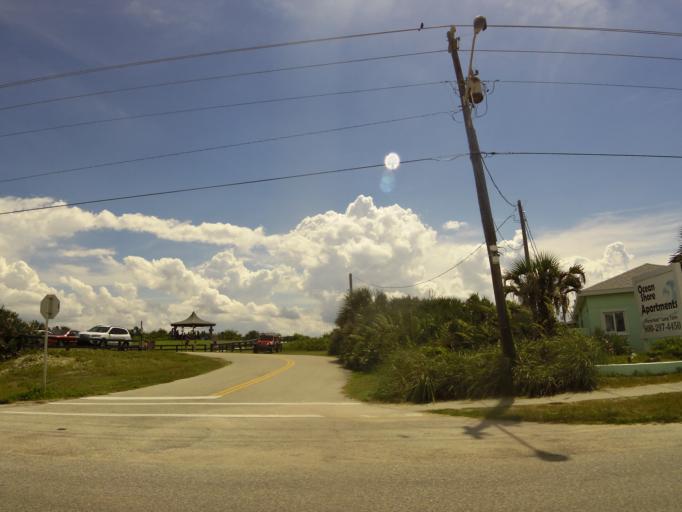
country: US
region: Florida
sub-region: Volusia County
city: Ormond-by-the-Sea
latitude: 29.3400
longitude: -81.0621
